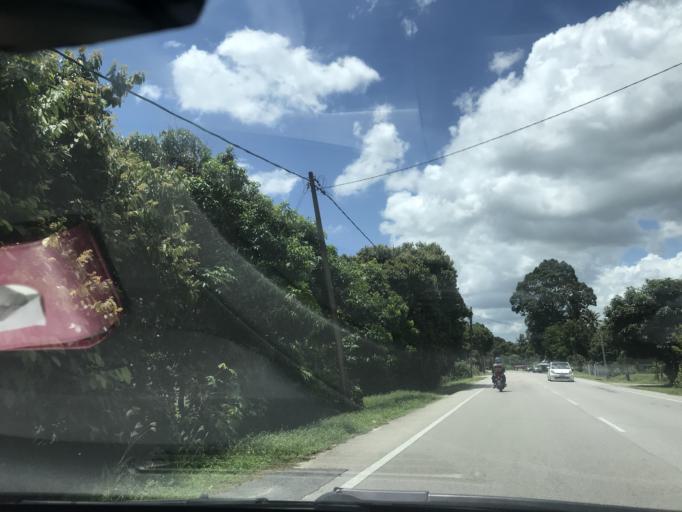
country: MY
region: Kelantan
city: Tumpat
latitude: 6.1795
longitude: 102.1785
